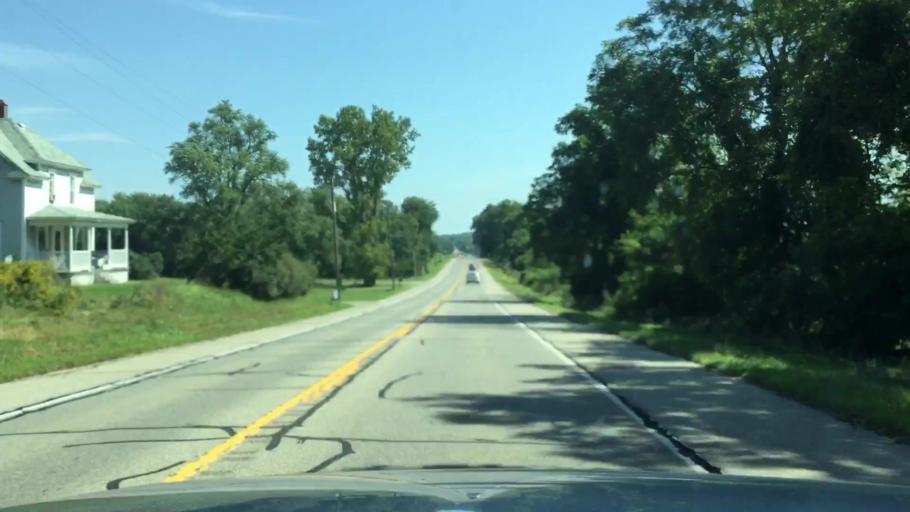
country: US
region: Michigan
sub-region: Lenawee County
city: Clinton
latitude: 42.0711
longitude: -84.0014
